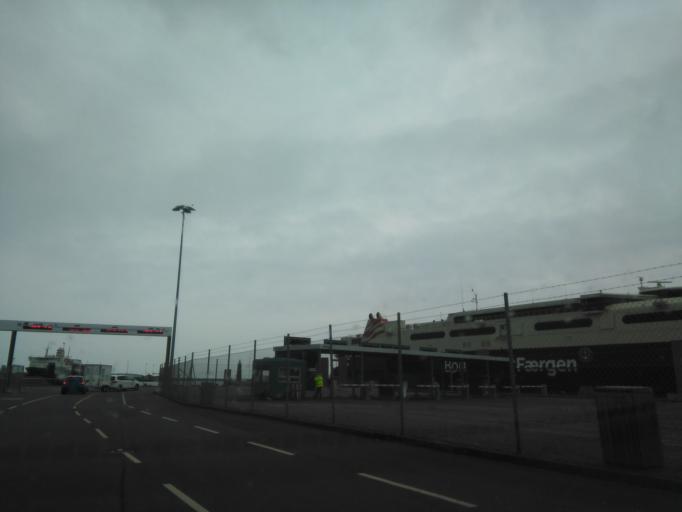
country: DK
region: Capital Region
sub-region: Bornholm Kommune
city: Ronne
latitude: 55.0999
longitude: 14.6928
